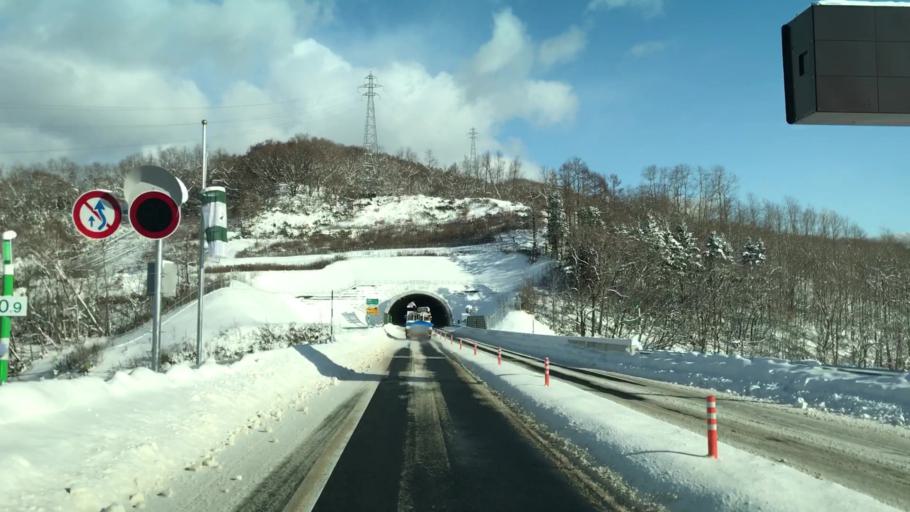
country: JP
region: Hokkaido
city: Yoichi
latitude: 43.1883
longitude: 140.8503
